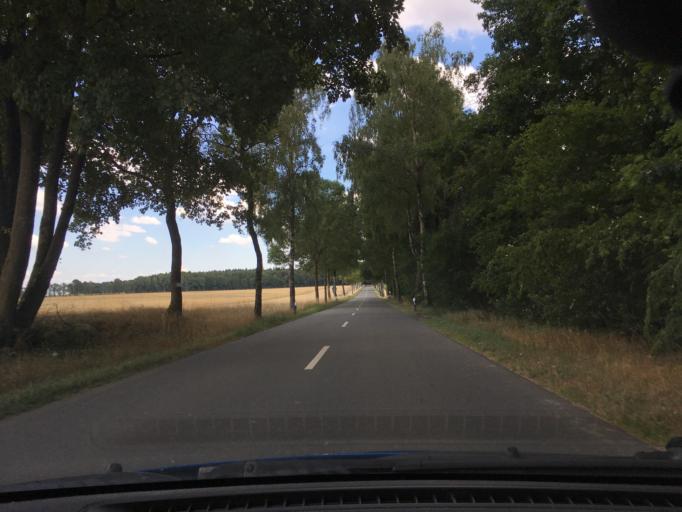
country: DE
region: Lower Saxony
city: Wriedel
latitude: 53.0527
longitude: 10.2490
